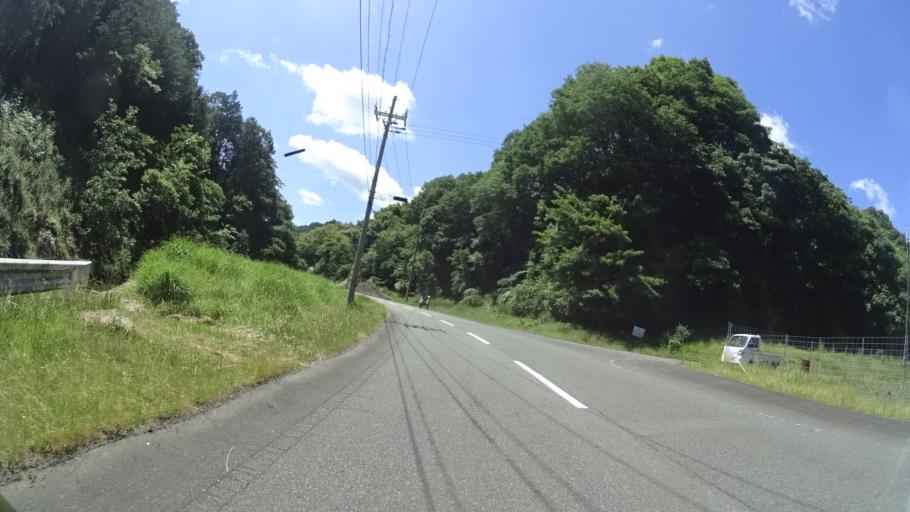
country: JP
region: Kyoto
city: Miyazu
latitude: 35.4188
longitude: 135.1855
